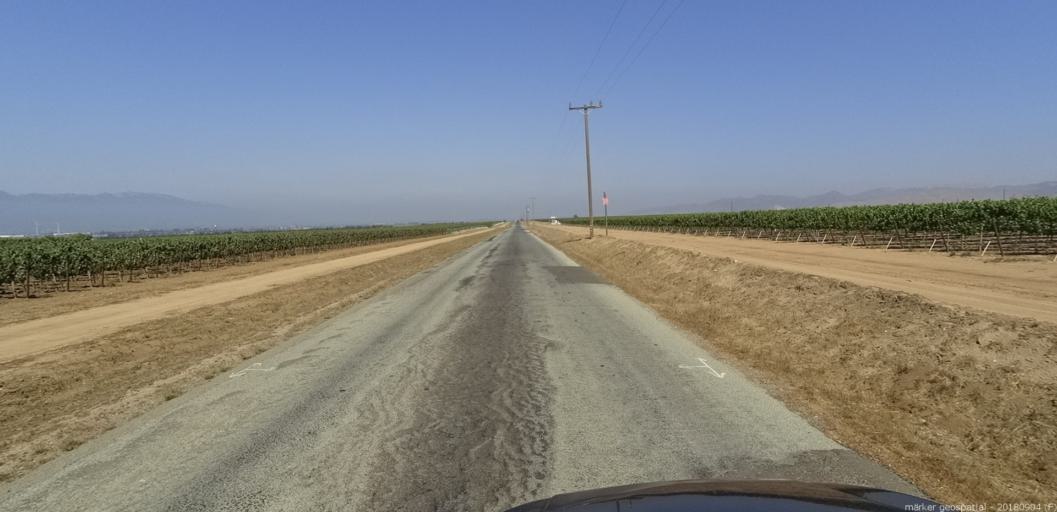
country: US
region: California
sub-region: Monterey County
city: Gonzales
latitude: 36.5046
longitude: -121.3987
